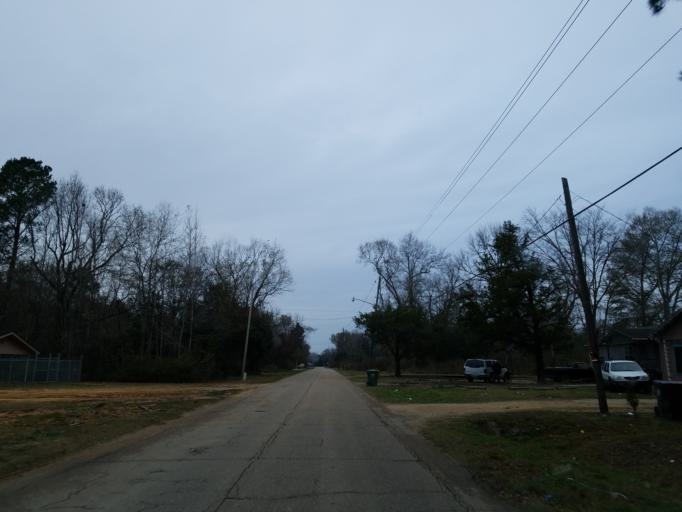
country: US
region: Mississippi
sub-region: Forrest County
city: Hattiesburg
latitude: 31.2943
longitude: -89.2699
